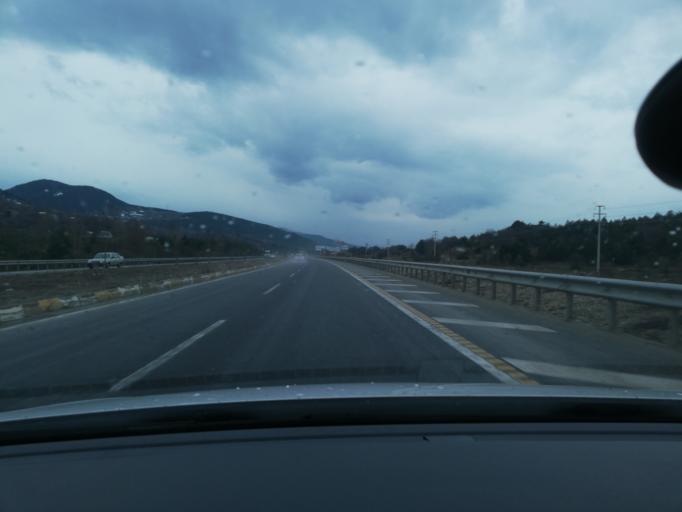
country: TR
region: Bolu
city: Yenicaga
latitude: 40.7561
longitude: 31.9147
